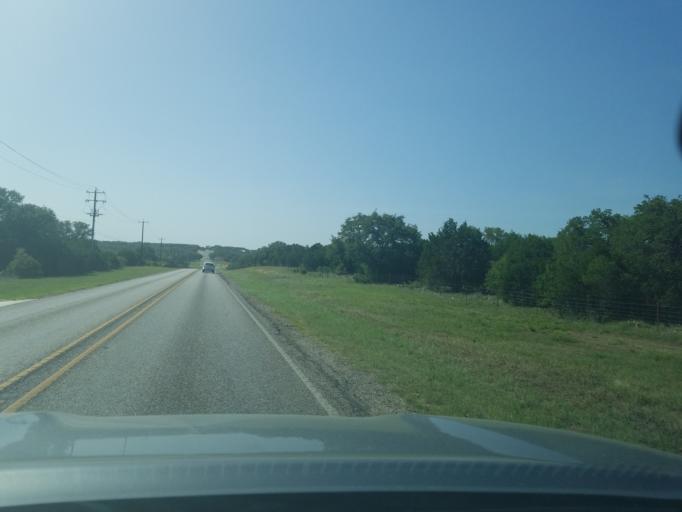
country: US
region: Texas
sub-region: Comal County
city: Garden Ridge
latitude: 29.6861
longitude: -98.3286
